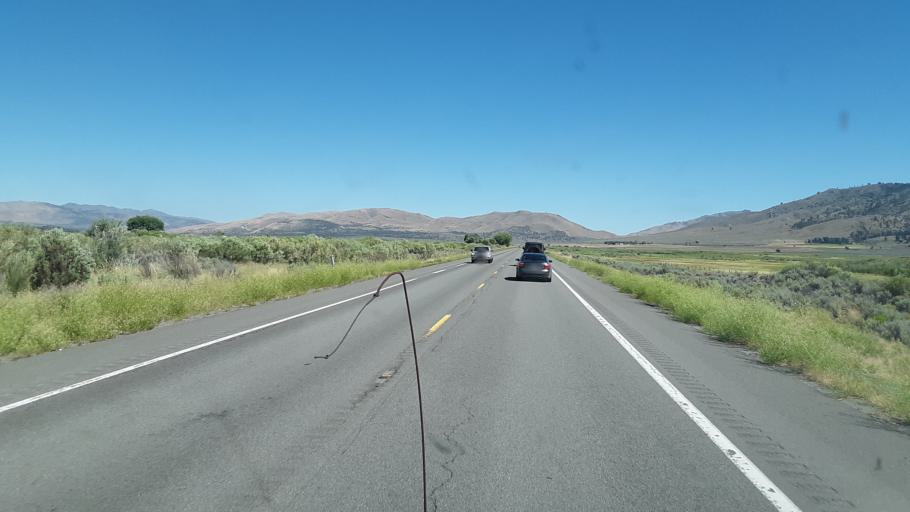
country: US
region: Nevada
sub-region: Washoe County
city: Cold Springs
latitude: 39.9799
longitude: -120.0625
